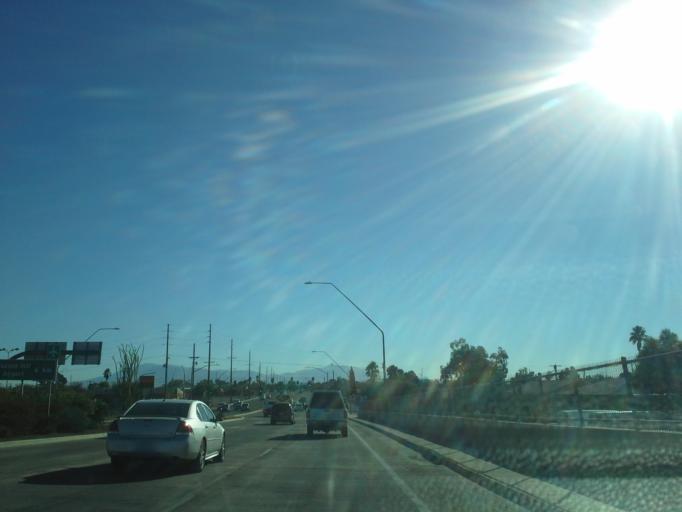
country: US
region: Arizona
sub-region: Pima County
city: Drexel Heights
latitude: 32.1338
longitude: -110.9841
